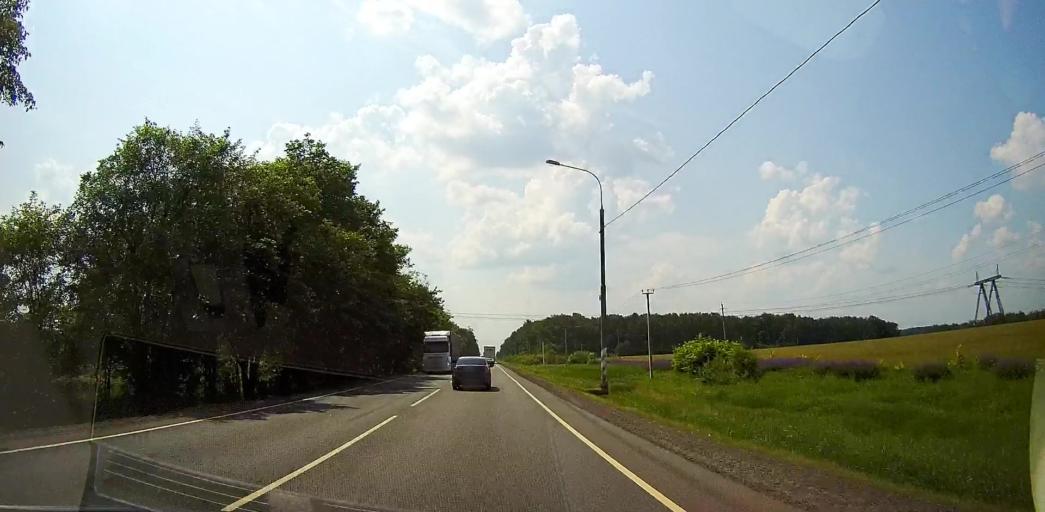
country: RU
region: Moskovskaya
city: Meshcherino
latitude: 55.1419
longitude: 38.2809
